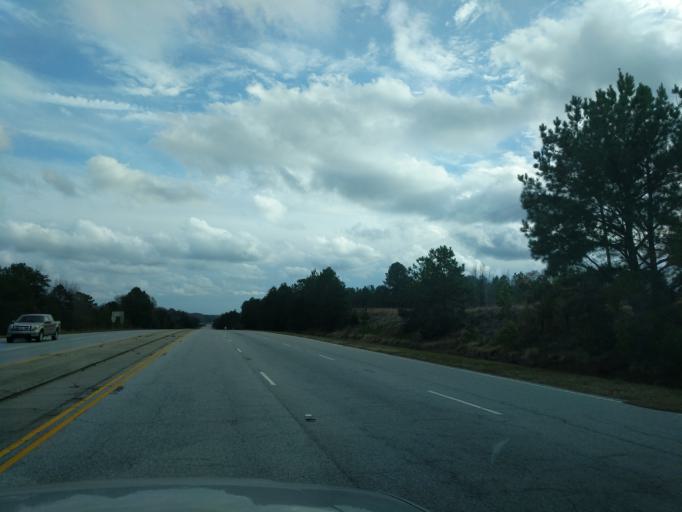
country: US
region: South Carolina
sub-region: Greenwood County
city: Ware Shoals
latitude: 34.4237
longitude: -82.2358
